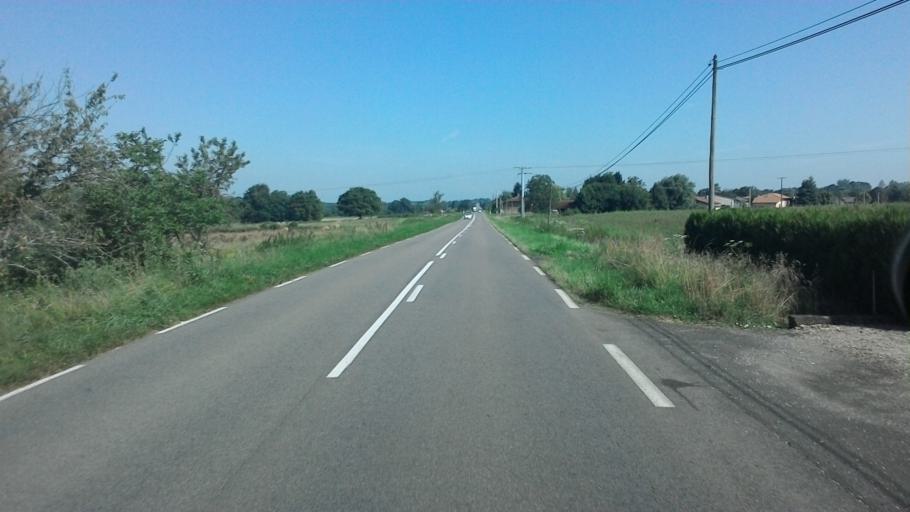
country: FR
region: Rhone-Alpes
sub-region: Departement de l'Ain
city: Saint-Trivier-de-Courtes
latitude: 46.4077
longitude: 5.1067
